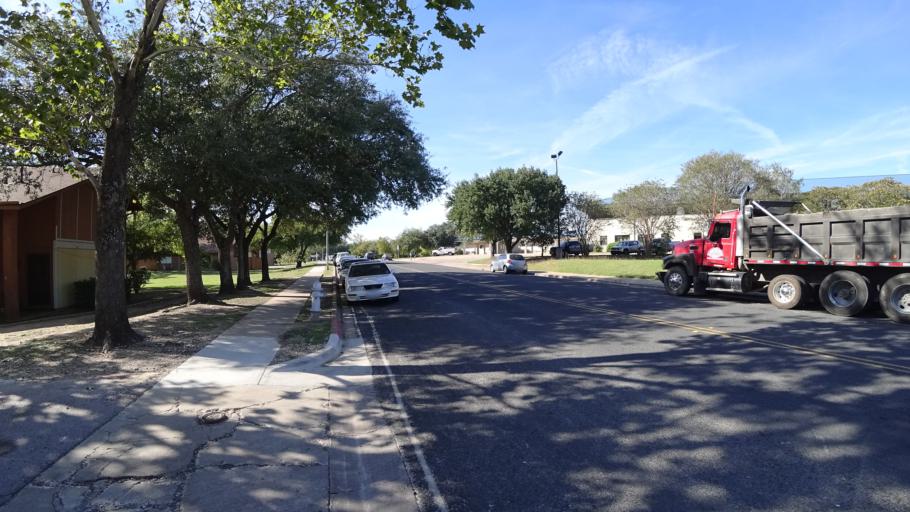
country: US
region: Texas
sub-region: Travis County
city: Onion Creek
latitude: 30.1879
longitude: -97.7437
